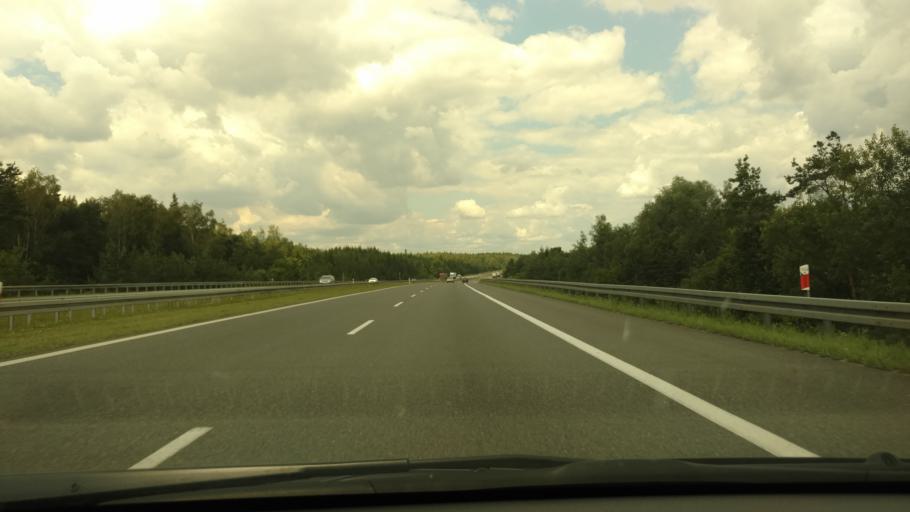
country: PL
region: Silesian Voivodeship
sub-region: Powiat bierunsko-ledzinski
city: Imielin
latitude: 50.1822
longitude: 19.1958
